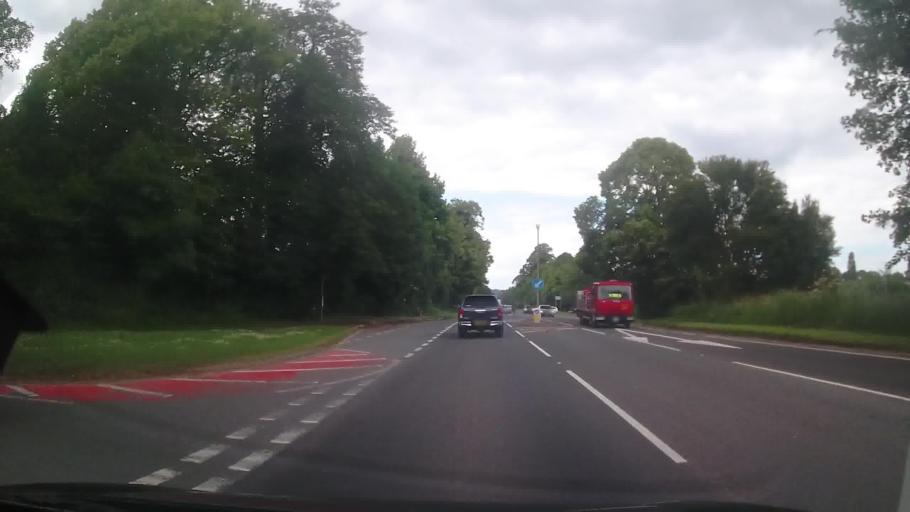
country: GB
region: England
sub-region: Herefordshire
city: Wellington
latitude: 52.1051
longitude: -2.7290
